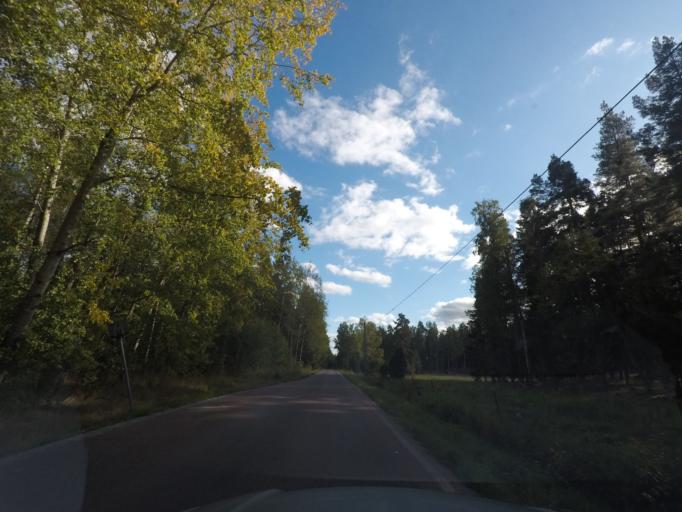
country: SE
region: Vaestmanland
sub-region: Hallstahammars Kommun
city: Kolback
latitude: 59.4952
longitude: 16.1899
